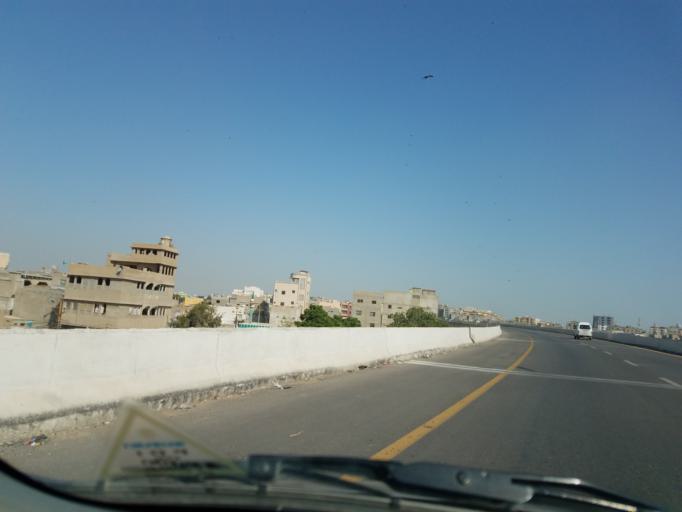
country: PK
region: Sindh
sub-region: Karachi District
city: Karachi
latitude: 24.8805
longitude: 67.0093
